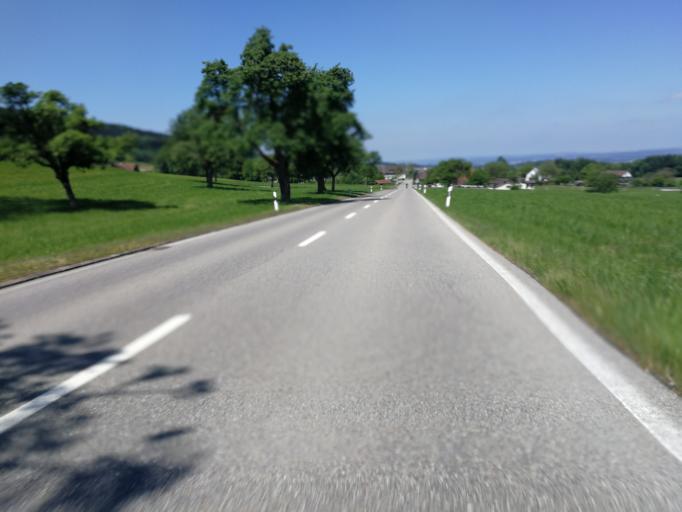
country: CH
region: Zurich
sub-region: Bezirk Uster
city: Esslingen
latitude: 47.2803
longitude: 8.6984
